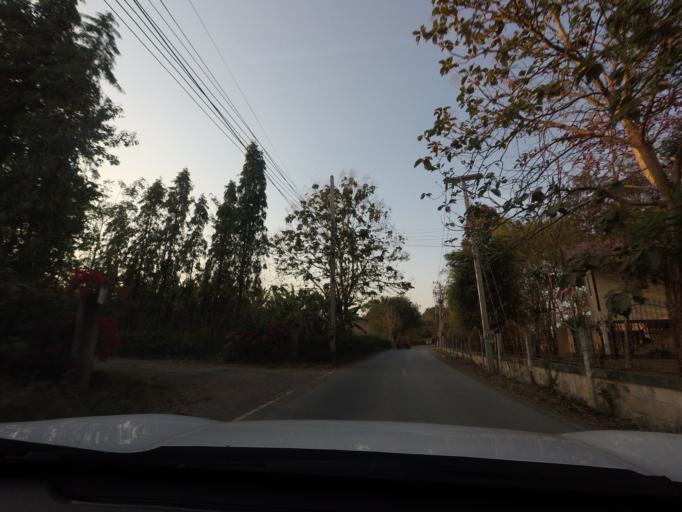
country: TH
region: Nakhon Ratchasima
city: Pak Chong
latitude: 14.6464
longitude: 101.4206
